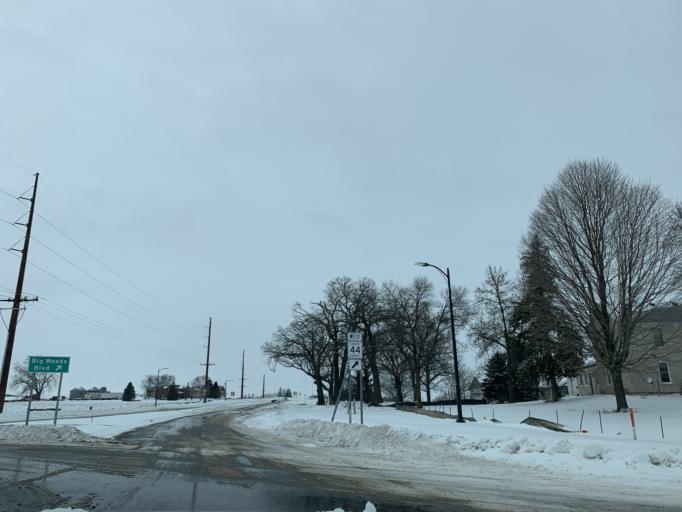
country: US
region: Minnesota
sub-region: Carver County
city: Chaska
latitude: 44.7912
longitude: -93.6253
